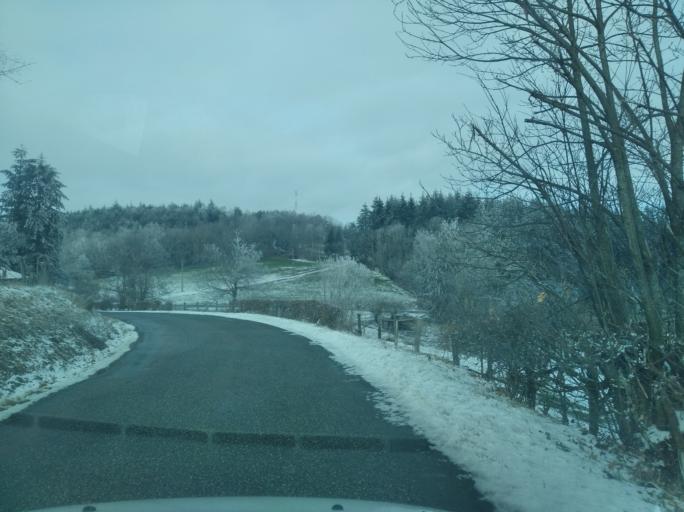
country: FR
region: Rhone-Alpes
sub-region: Departement de la Loire
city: La Pacaudiere
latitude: 46.1370
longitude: 3.7996
